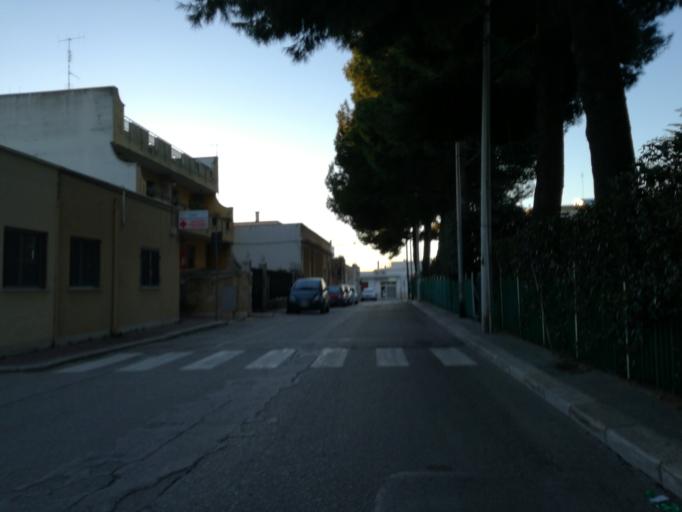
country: IT
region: Apulia
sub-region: Provincia di Bari
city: Adelfia
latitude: 41.0002
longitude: 16.8773
